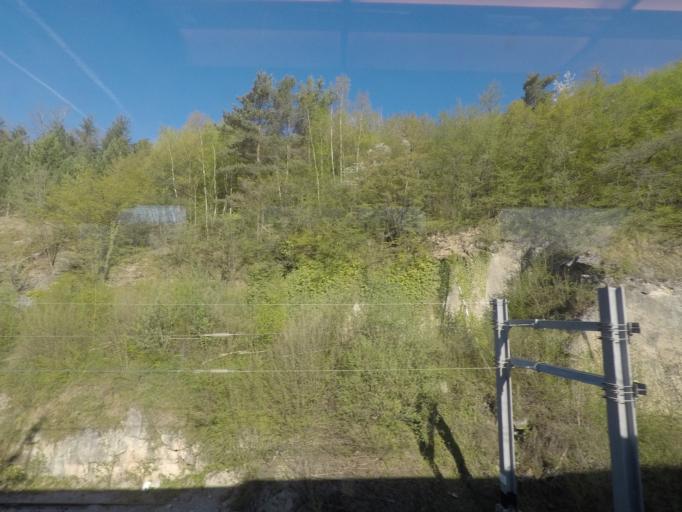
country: BE
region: Wallonia
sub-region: Province de Namur
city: Rochefort
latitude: 50.1672
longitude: 5.2712
